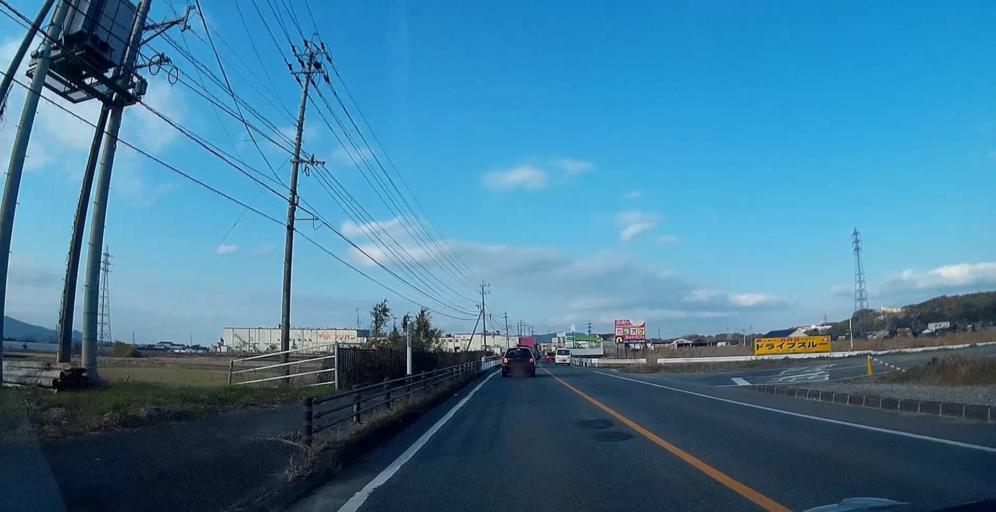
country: JP
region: Kumamoto
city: Matsubase
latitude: 32.6185
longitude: 130.7044
